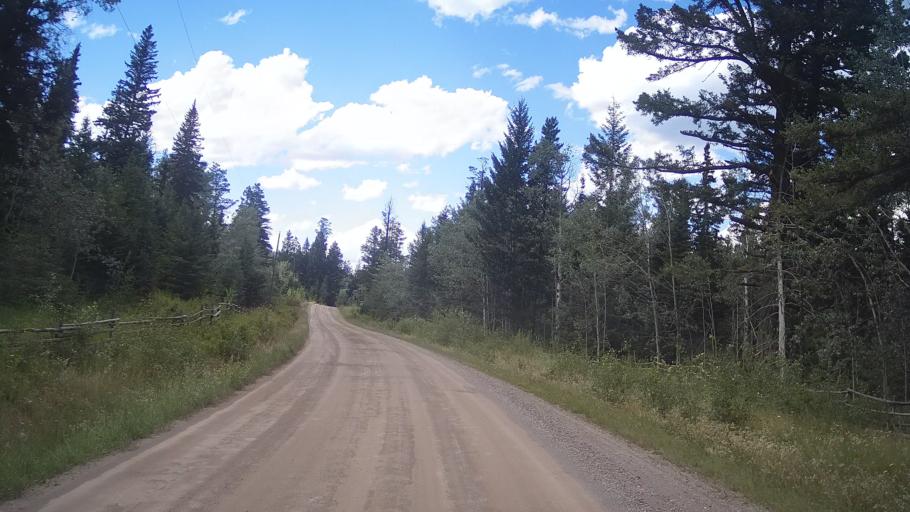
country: CA
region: British Columbia
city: Lillooet
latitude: 51.3083
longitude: -121.8208
